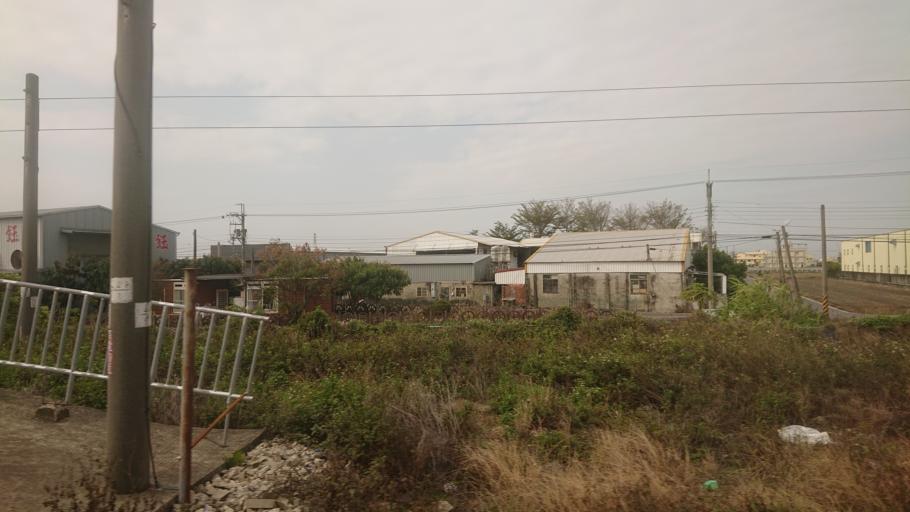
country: TW
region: Taiwan
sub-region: Changhua
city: Chang-hua
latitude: 24.0261
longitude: 120.5366
